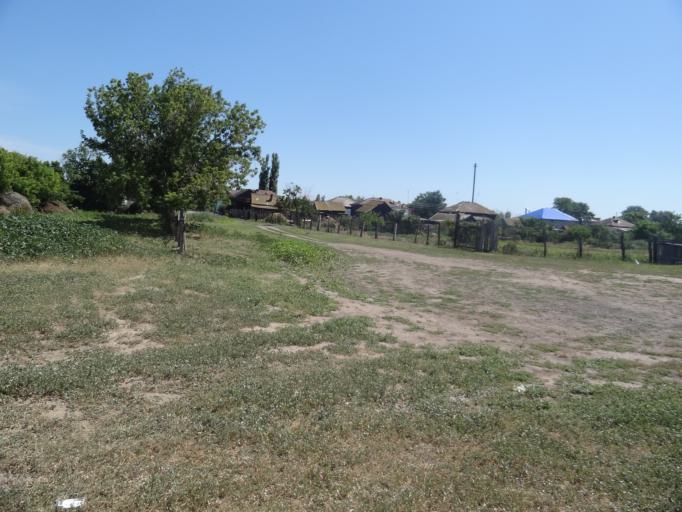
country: RU
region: Saratov
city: Krasnoarmeysk
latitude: 51.0877
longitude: 45.9431
